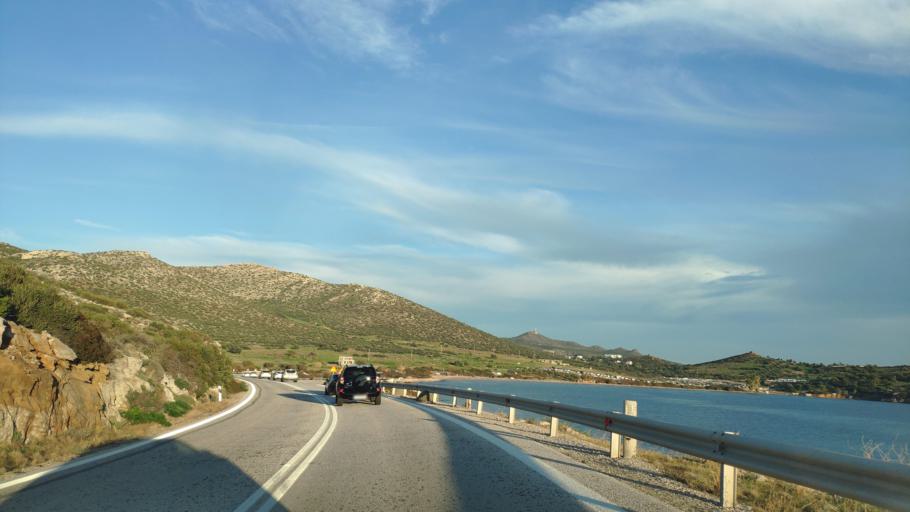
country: GR
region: Attica
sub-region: Nomarchia Anatolikis Attikis
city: Palaia Fokaia
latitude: 37.6658
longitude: 23.9649
